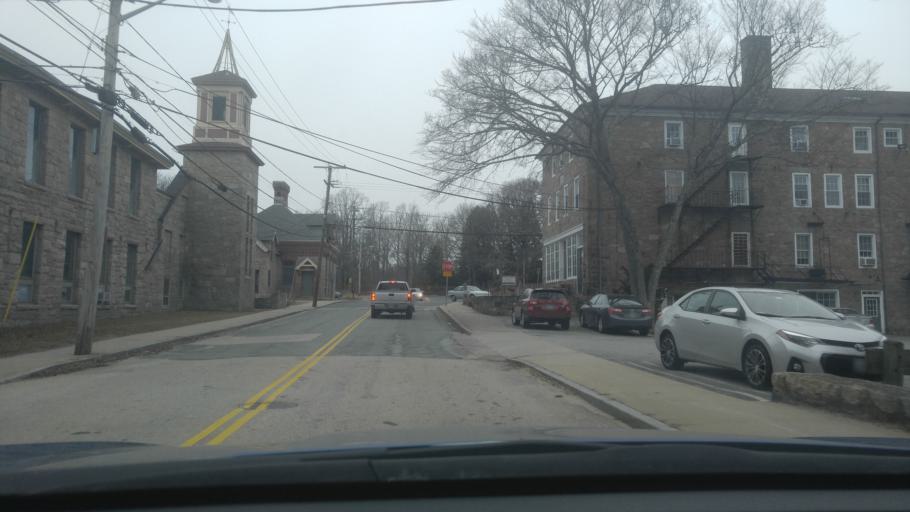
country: US
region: Rhode Island
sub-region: Washington County
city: Wakefield-Peacedale
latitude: 41.4500
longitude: -71.4957
